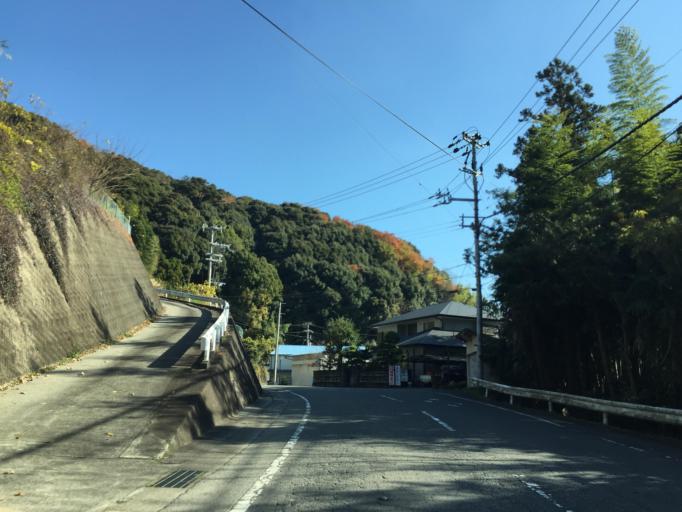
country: JP
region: Wakayama
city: Iwade
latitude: 34.1509
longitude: 135.3709
